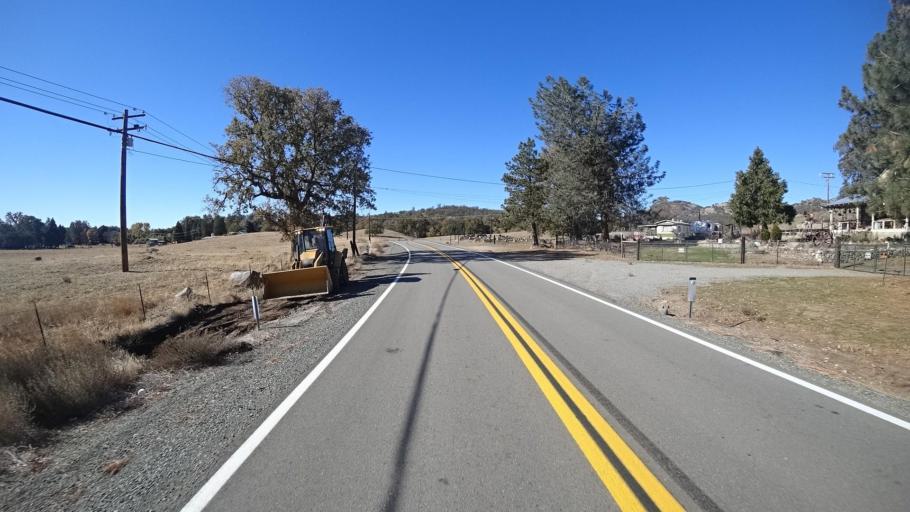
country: US
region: California
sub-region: Kern County
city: Alta Sierra
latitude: 35.7261
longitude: -118.7207
